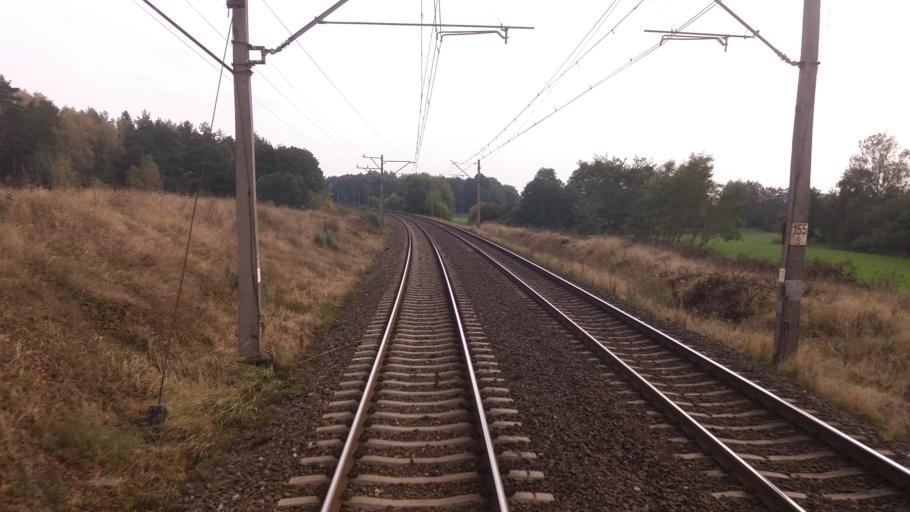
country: PL
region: West Pomeranian Voivodeship
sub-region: Powiat stargardzki
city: Dolice
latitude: 53.2095
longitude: 15.1694
